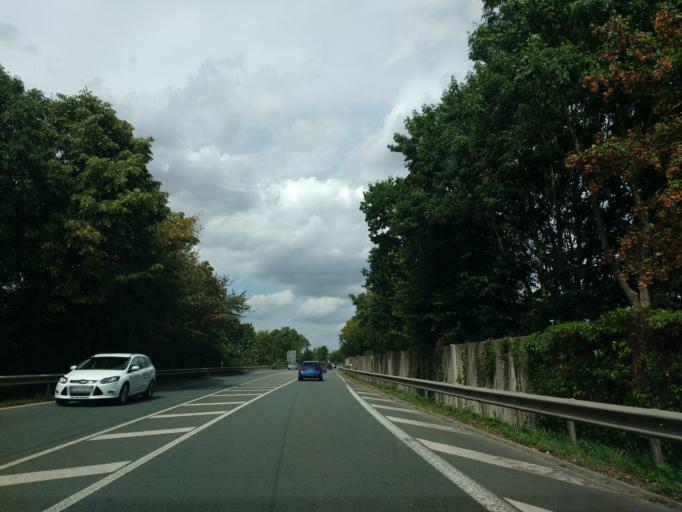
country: DE
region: North Rhine-Westphalia
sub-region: Regierungsbezirk Detmold
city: Petershagen
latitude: 52.3387
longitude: 8.9613
